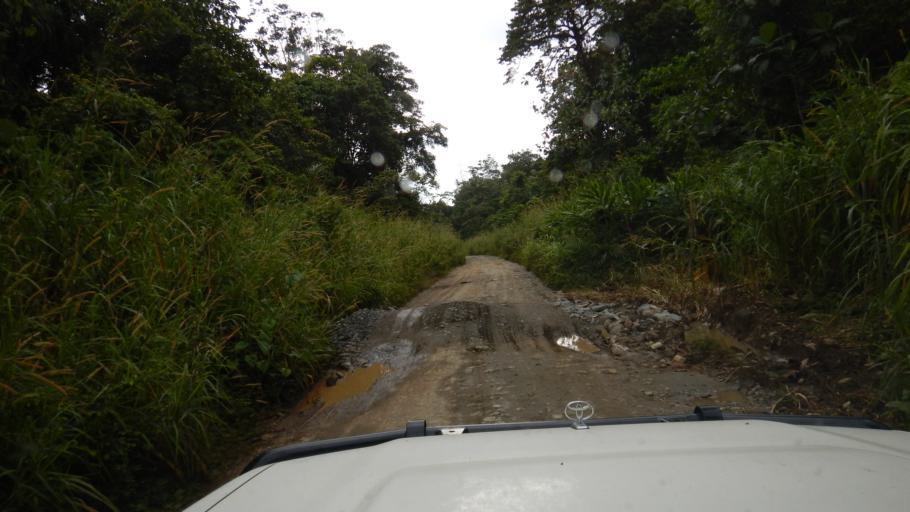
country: PG
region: Northern Province
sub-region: Sohe
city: Kokoda
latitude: -8.9056
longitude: 147.8194
